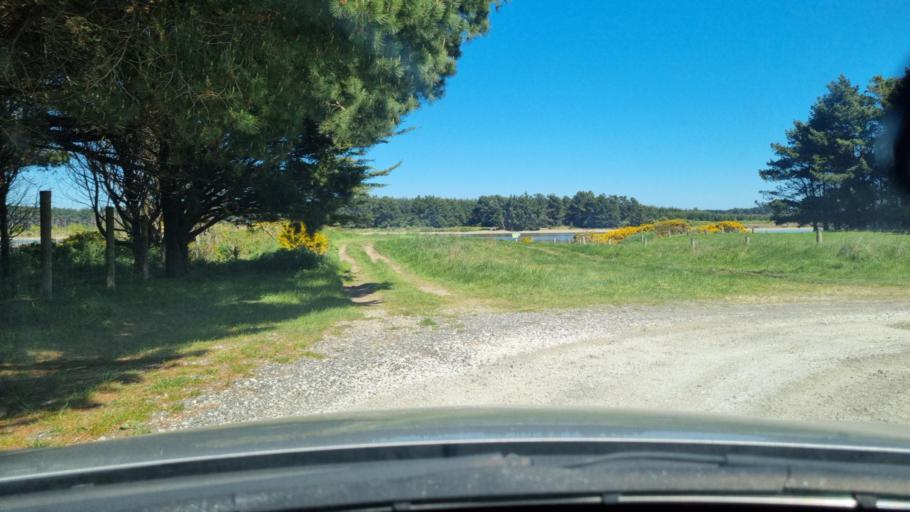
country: NZ
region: Southland
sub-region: Invercargill City
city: Invercargill
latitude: -46.4586
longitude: 168.2701
